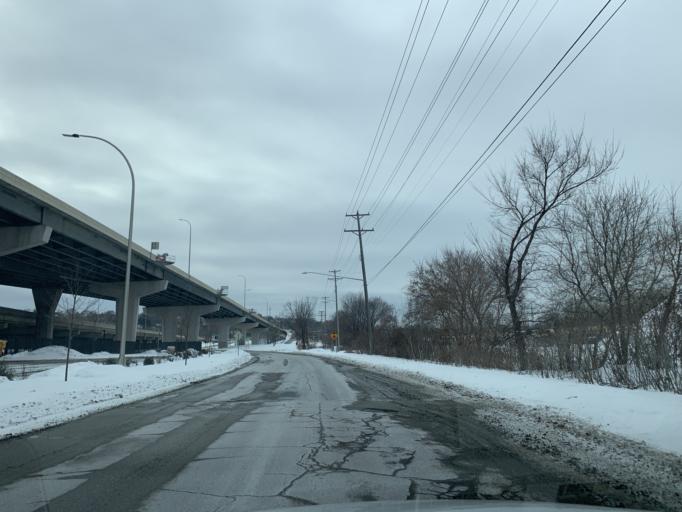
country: US
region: Minnesota
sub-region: Hennepin County
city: Minneapolis
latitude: 44.9747
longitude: -93.2926
